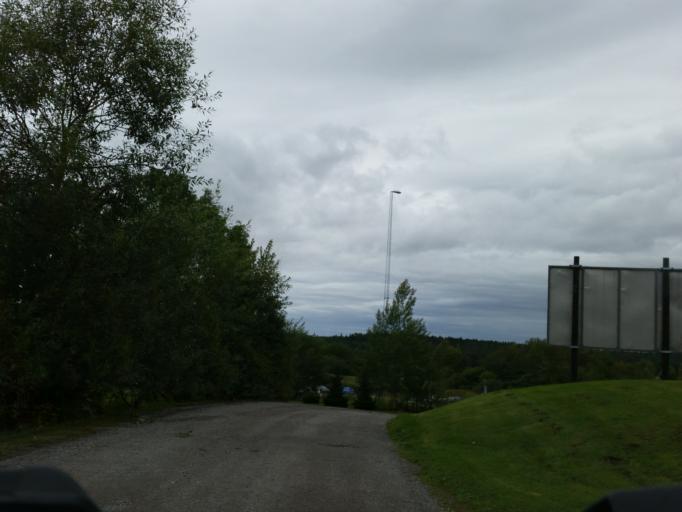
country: SE
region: Uppsala
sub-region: Enkopings Kommun
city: Grillby
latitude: 59.6349
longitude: 17.2691
